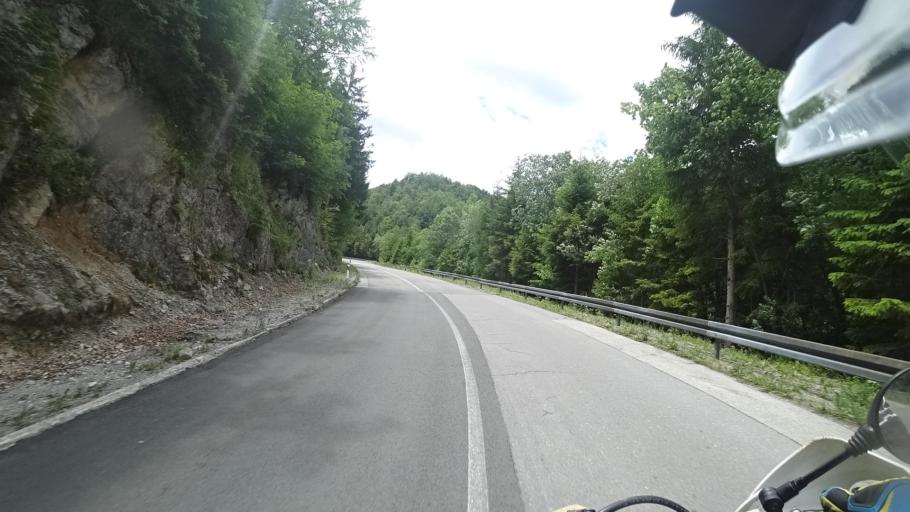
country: SI
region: Osilnica
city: Osilnica
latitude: 45.5987
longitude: 14.6329
